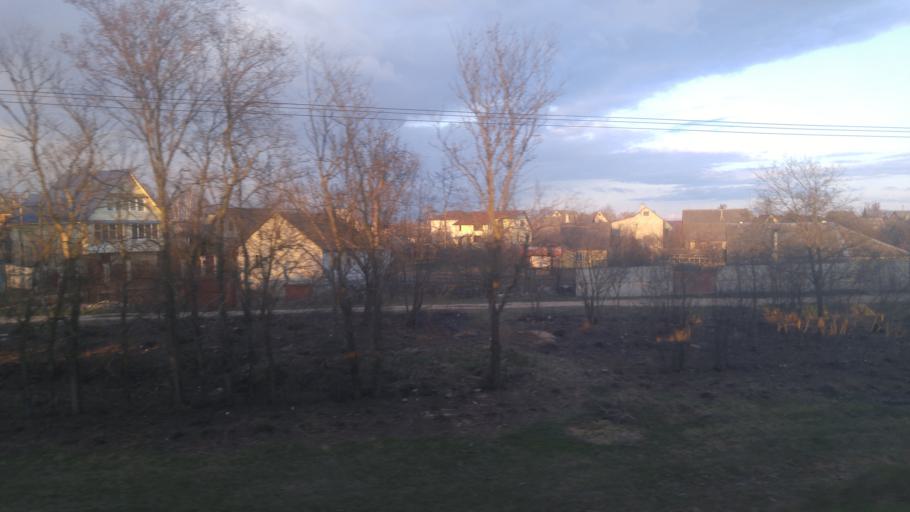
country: BY
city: Michanovichi
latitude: 53.6755
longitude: 27.7480
